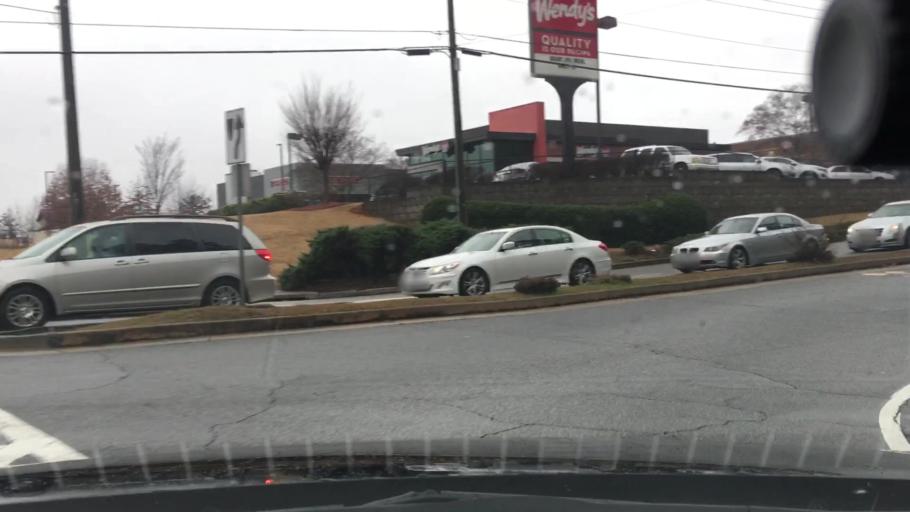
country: US
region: Georgia
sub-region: Coweta County
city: East Newnan
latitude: 33.3982
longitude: -84.7388
